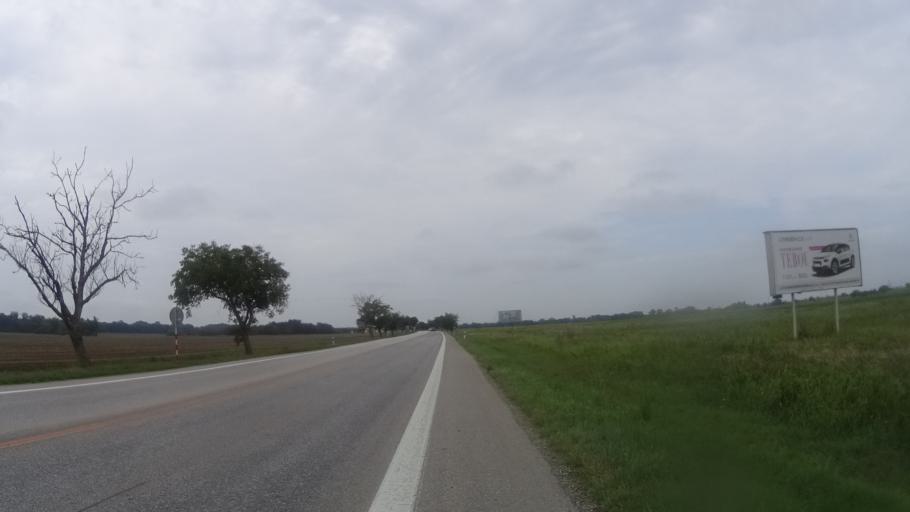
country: SK
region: Nitriansky
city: Komarno
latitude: 47.7656
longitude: 18.0811
